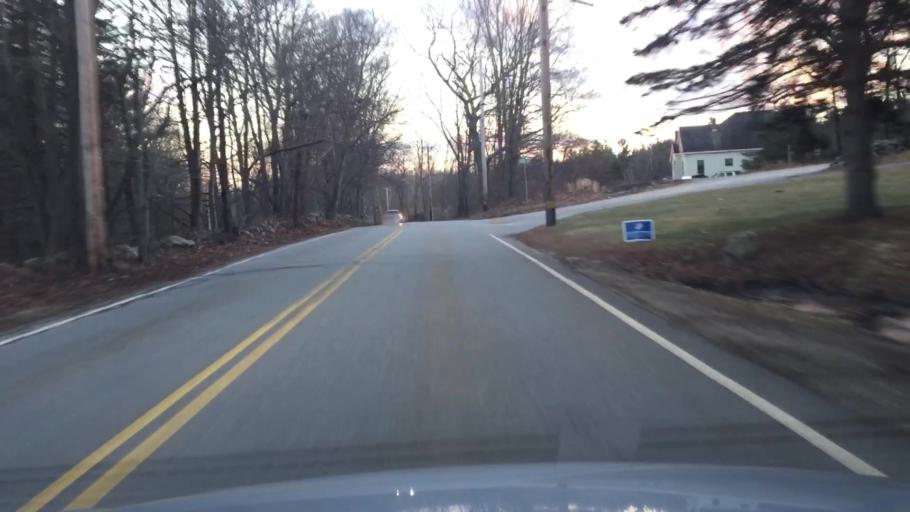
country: US
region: Massachusetts
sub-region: Worcester County
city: Princeton
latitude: 42.4411
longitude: -71.8316
